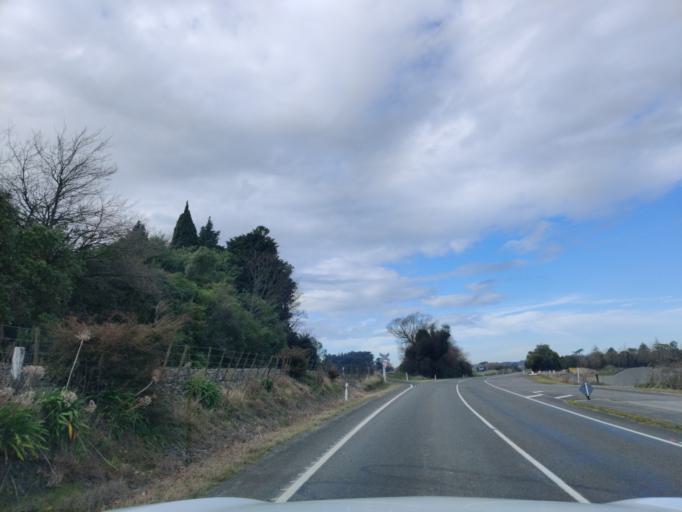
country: NZ
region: Manawatu-Wanganui
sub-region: Palmerston North City
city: Palmerston North
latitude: -40.3366
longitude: 175.8325
